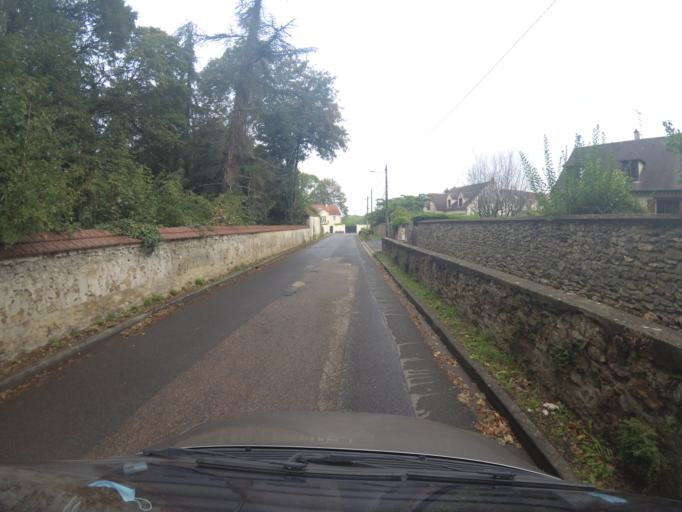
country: FR
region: Ile-de-France
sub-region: Departement de Seine-et-Marne
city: Conches-sur-Gondoire
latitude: 48.8550
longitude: 2.7147
